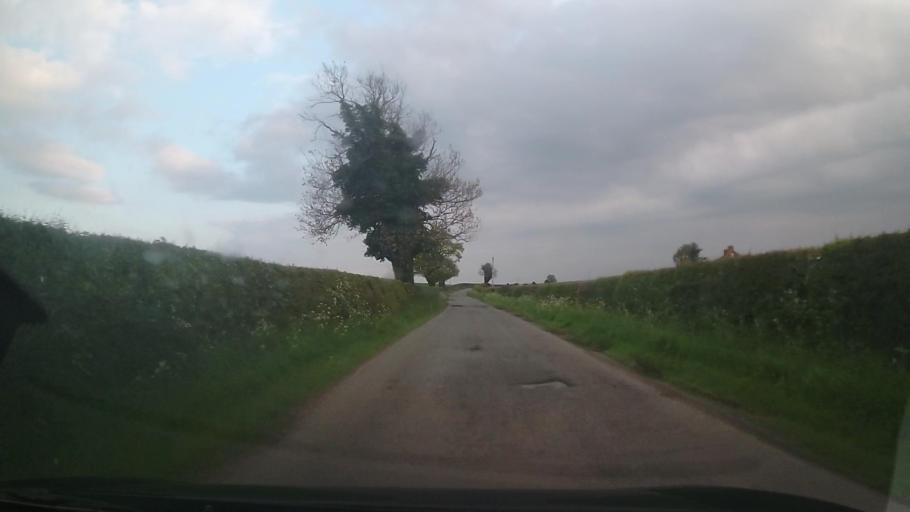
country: GB
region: England
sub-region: Shropshire
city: Ellesmere
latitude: 52.9111
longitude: -2.8043
